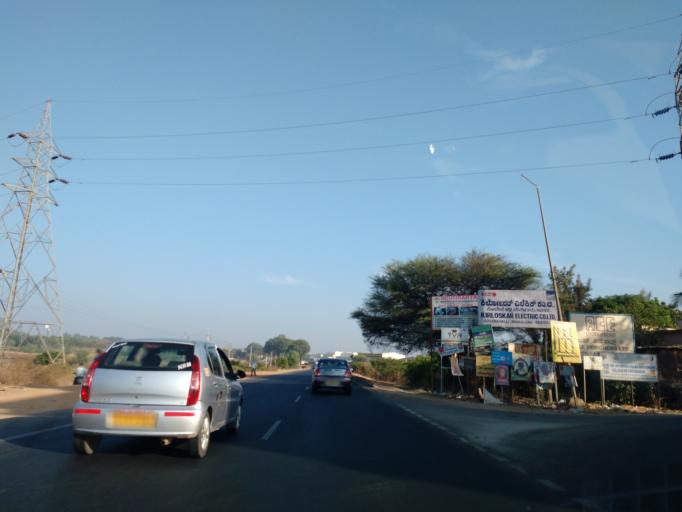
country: IN
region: Karnataka
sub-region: Bangalore Rural
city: Nelamangala
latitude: 13.1501
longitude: 77.3373
